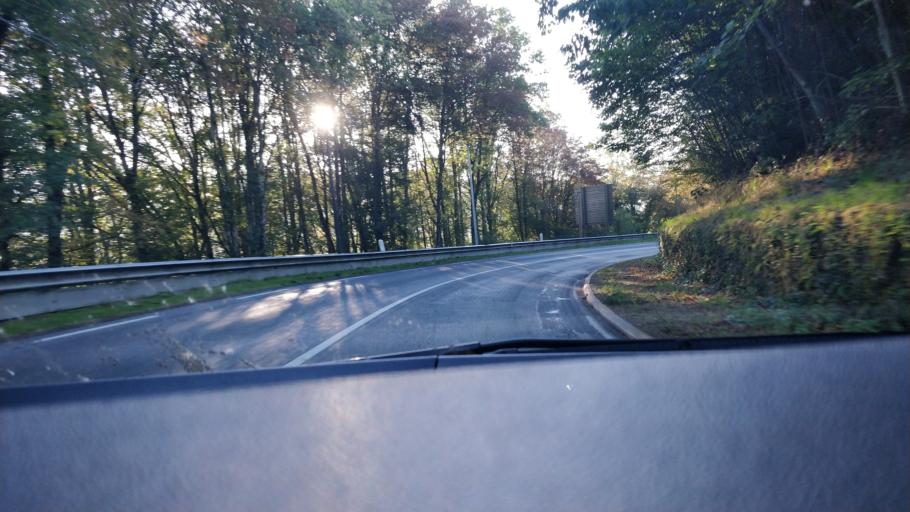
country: FR
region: Limousin
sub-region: Departement de la Creuse
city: Bourganeuf
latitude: 45.9596
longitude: 1.7402
